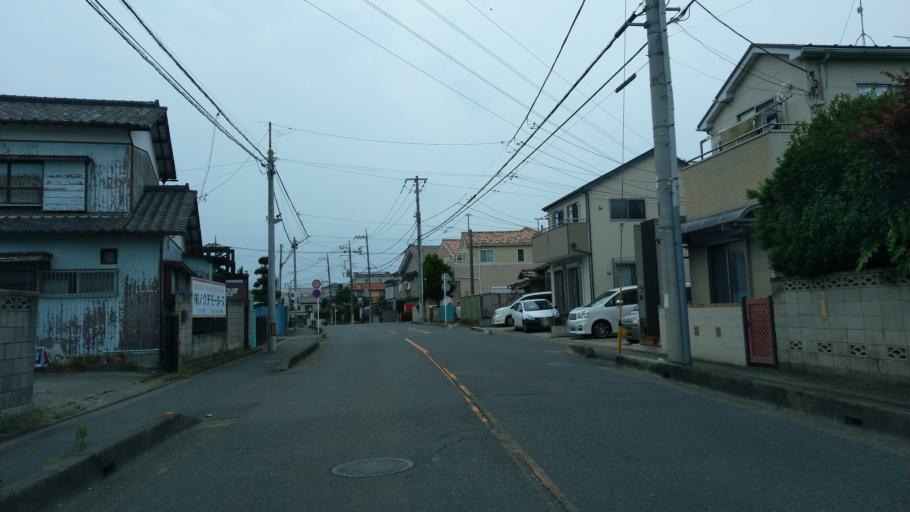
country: JP
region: Saitama
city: Saitama
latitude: 35.8670
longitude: 139.6775
